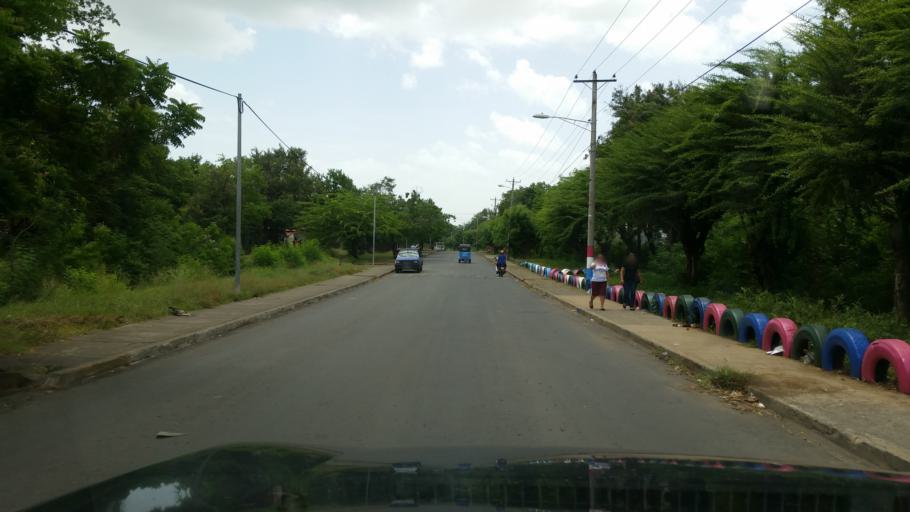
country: NI
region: Managua
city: Managua
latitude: 12.1323
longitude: -86.2198
